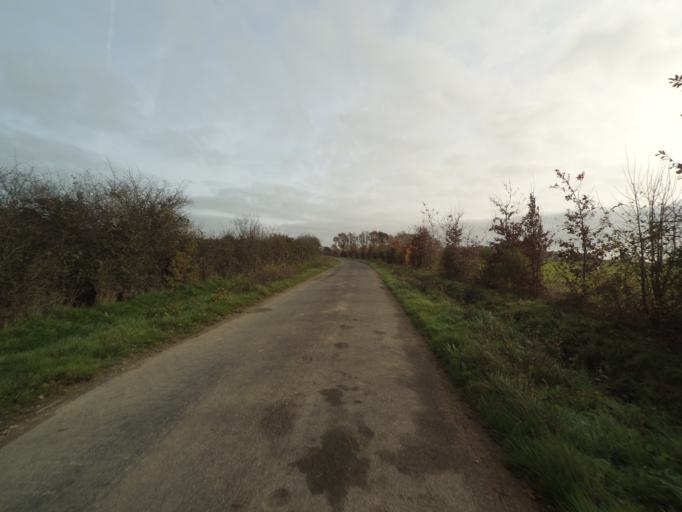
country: FR
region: Pays de la Loire
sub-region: Departement de la Loire-Atlantique
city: La Planche
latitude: 47.0145
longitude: -1.4030
